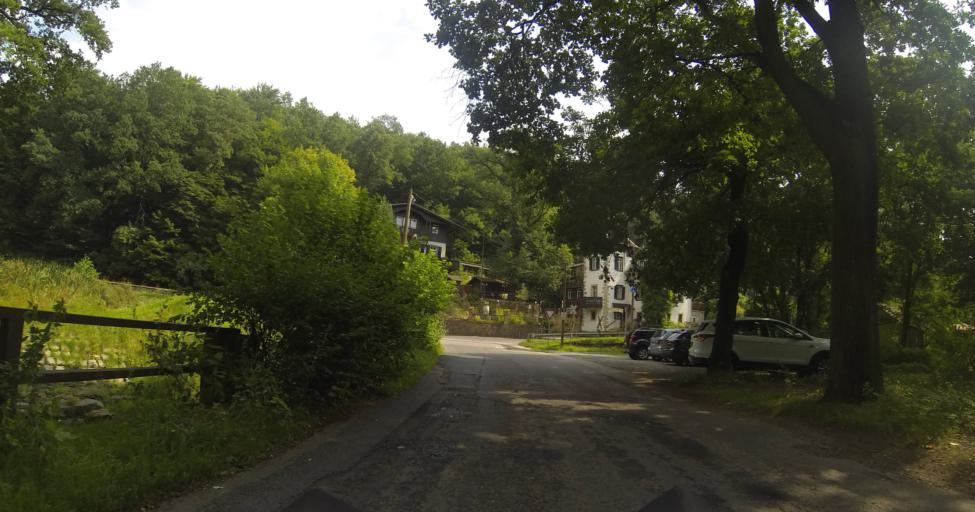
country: DE
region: Saxony
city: Radebeul
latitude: 51.1227
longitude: 13.6534
